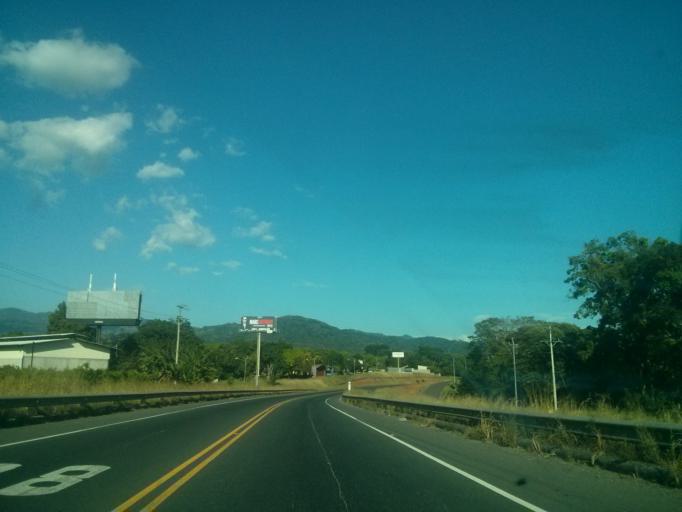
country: CR
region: Alajuela
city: Orotina
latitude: 9.9099
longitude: -84.5140
